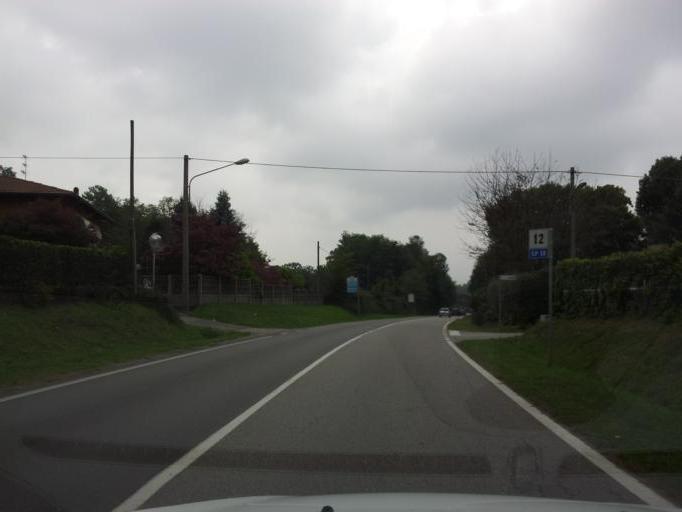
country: IT
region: Lombardy
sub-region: Provincia di Varese
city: Corgeno
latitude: 45.7451
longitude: 8.6900
